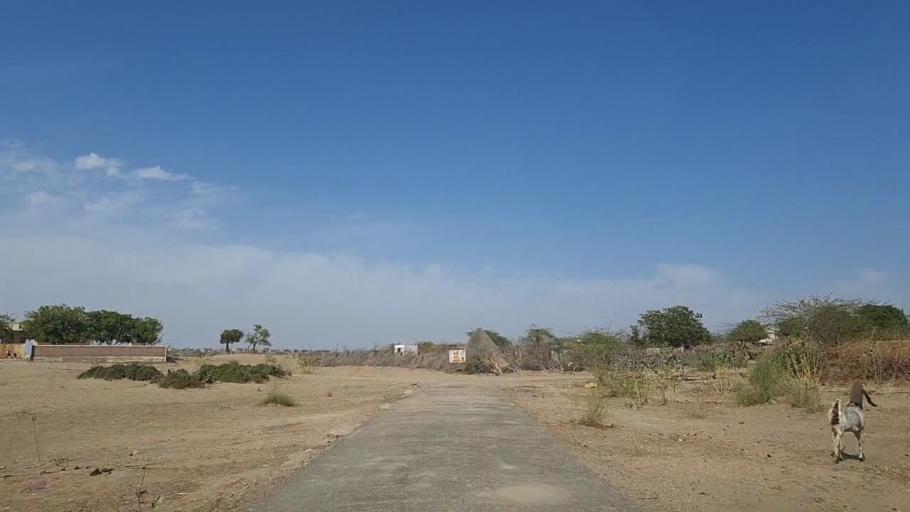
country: PK
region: Sindh
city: Nabisar
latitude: 24.8818
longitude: 69.6138
